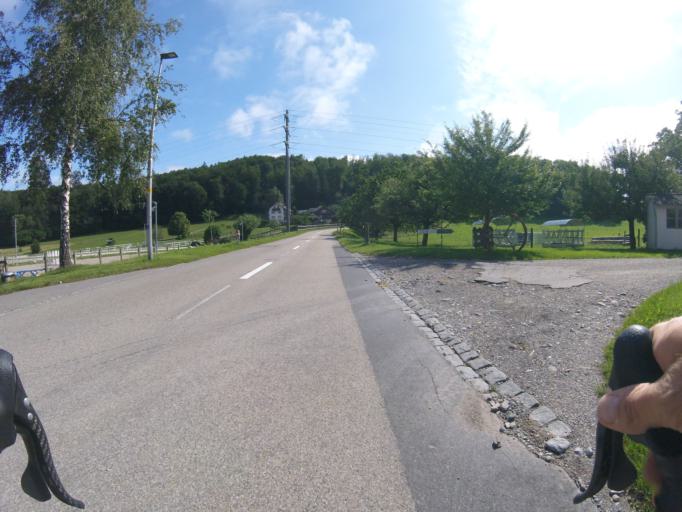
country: CH
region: Bern
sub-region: Bern-Mittelland District
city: Worb
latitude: 46.9331
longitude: 7.5726
